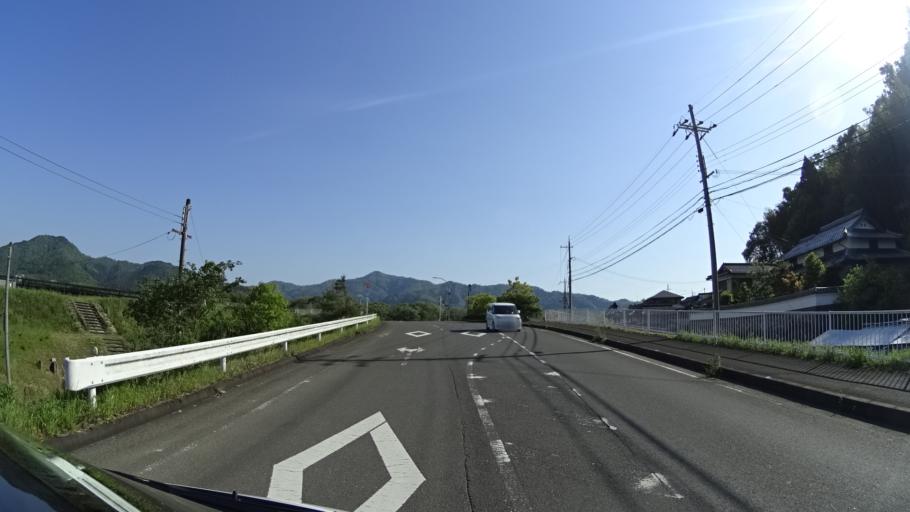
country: JP
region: Kyoto
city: Ayabe
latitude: 35.3119
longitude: 135.2080
